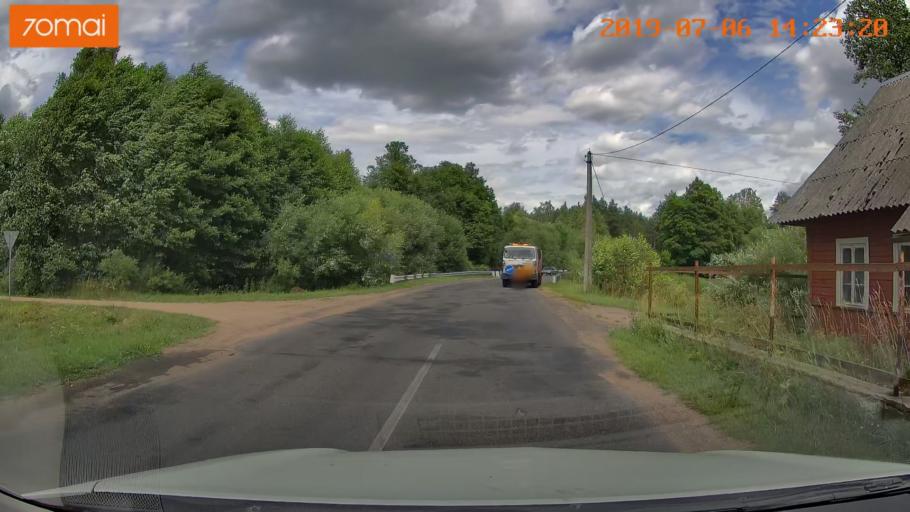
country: BY
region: Minsk
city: Ivyanyets
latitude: 53.9181
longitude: 26.7689
